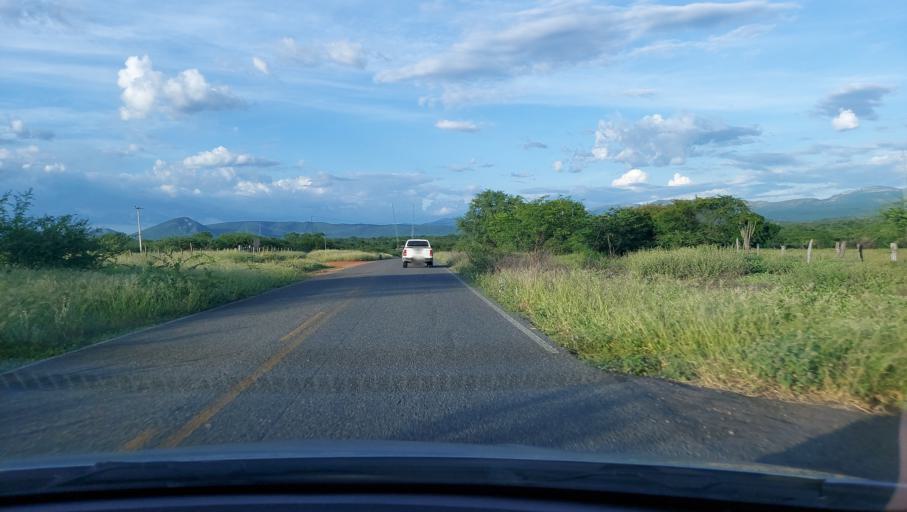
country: BR
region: Bahia
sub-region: Oliveira Dos Brejinhos
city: Beira Rio
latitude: -12.1983
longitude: -42.5382
